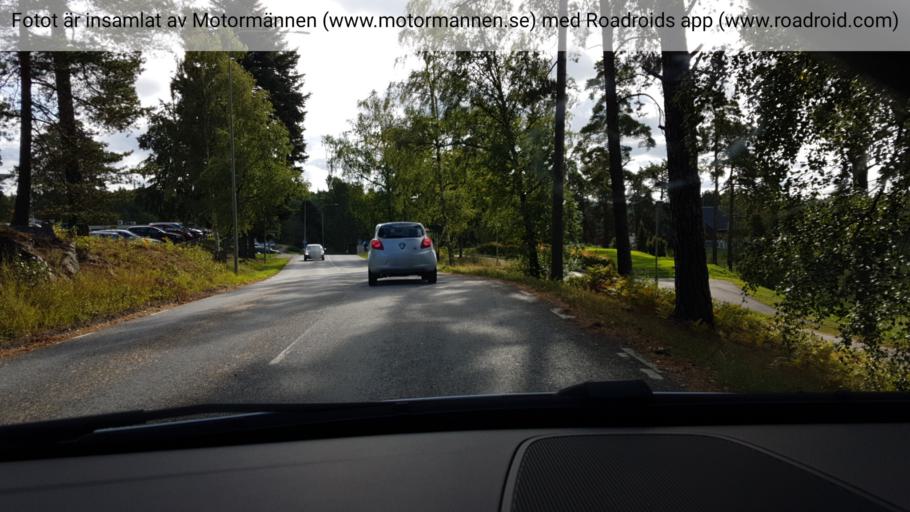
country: SE
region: Stockholm
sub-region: Lidingo
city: Lidingoe
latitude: 59.3797
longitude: 18.1246
